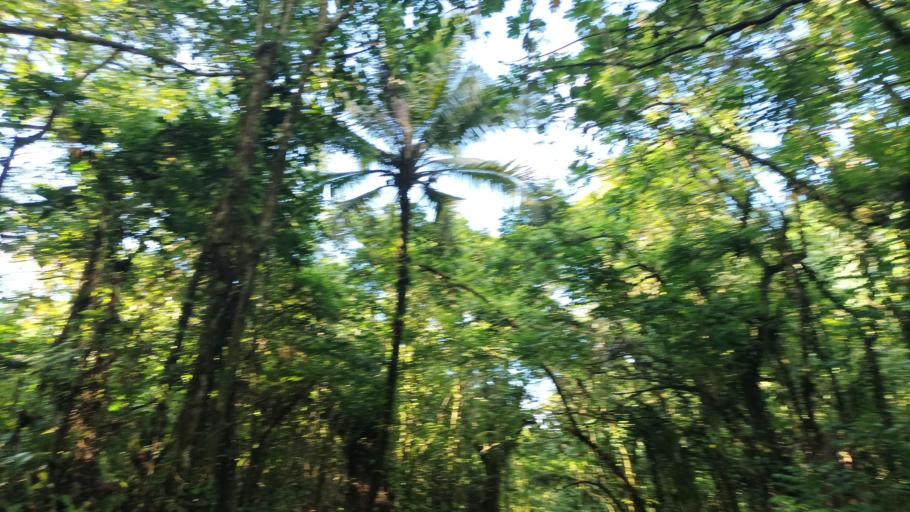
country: FM
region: Pohnpei
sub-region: Kolonia Municipality
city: Kolonia Town
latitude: 6.9674
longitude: 158.1863
